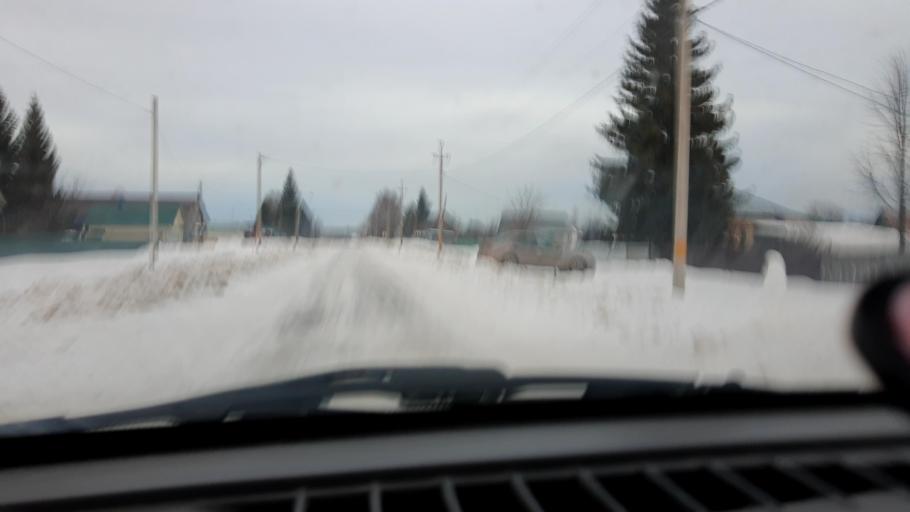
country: RU
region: Bashkortostan
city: Urman
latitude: 54.8688
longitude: 56.8666
